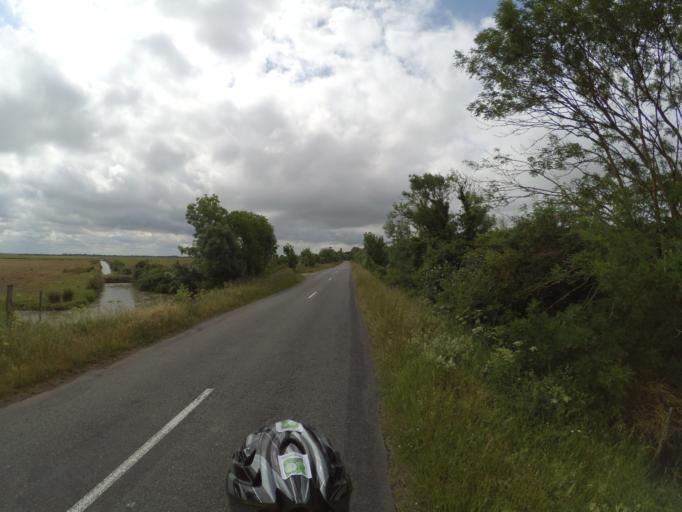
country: FR
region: Poitou-Charentes
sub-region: Departement de la Charente-Maritime
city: Yves
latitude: 46.0242
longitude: -1.0469
